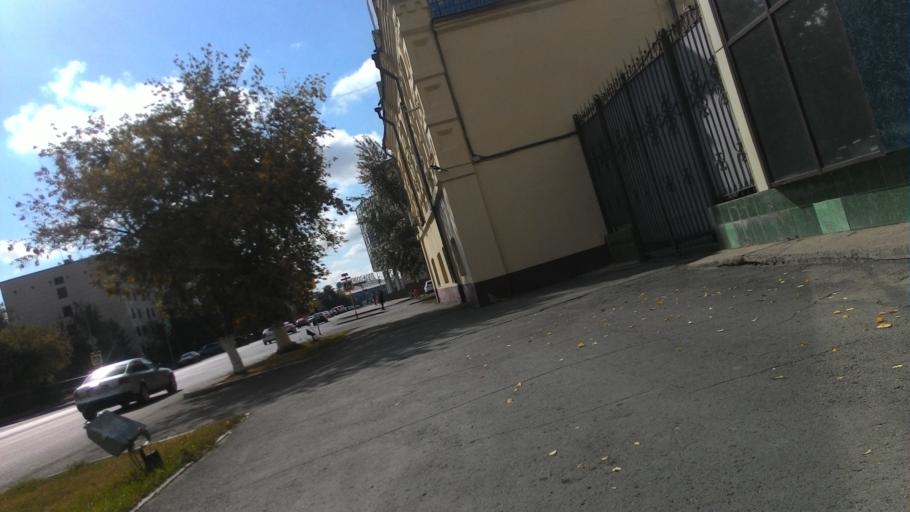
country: KZ
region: Astana Qalasy
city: Astana
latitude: 51.1697
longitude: 71.4201
